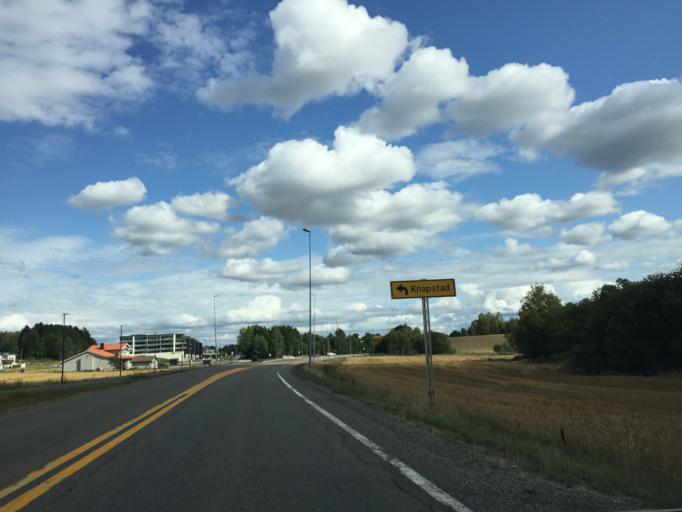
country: NO
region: Ostfold
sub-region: Hobol
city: Knappstad
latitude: 59.6201
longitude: 11.0191
